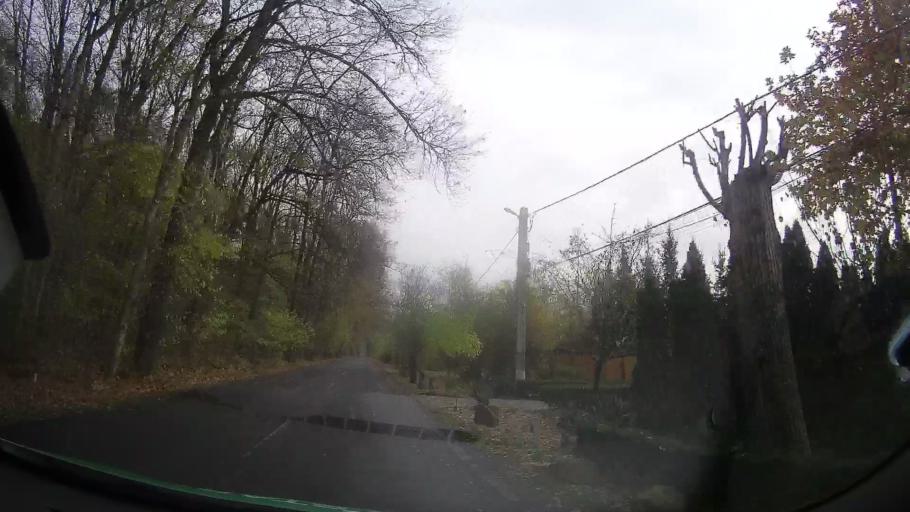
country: RO
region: Ilfov
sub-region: Comuna Snagov
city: Snagov
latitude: 44.7161
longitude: 26.1910
